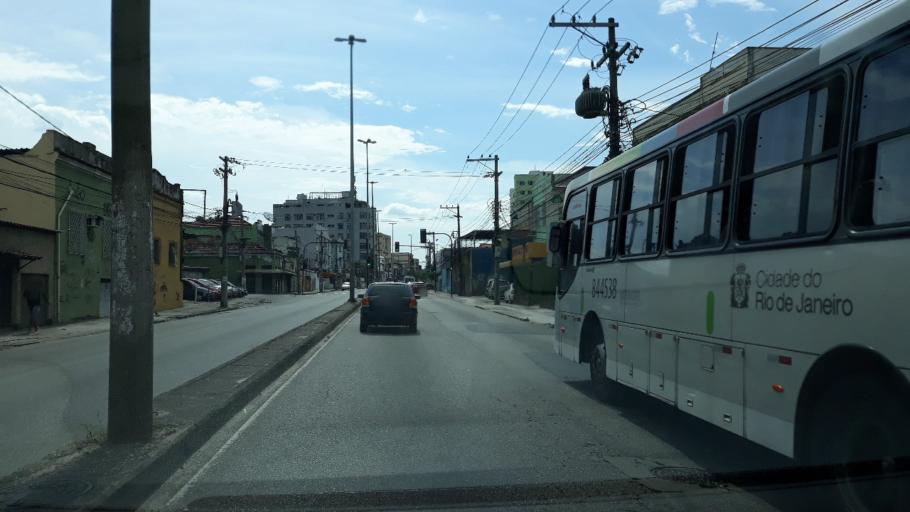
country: BR
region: Rio de Janeiro
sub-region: Duque De Caxias
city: Duque de Caxias
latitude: -22.8850
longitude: -43.3123
